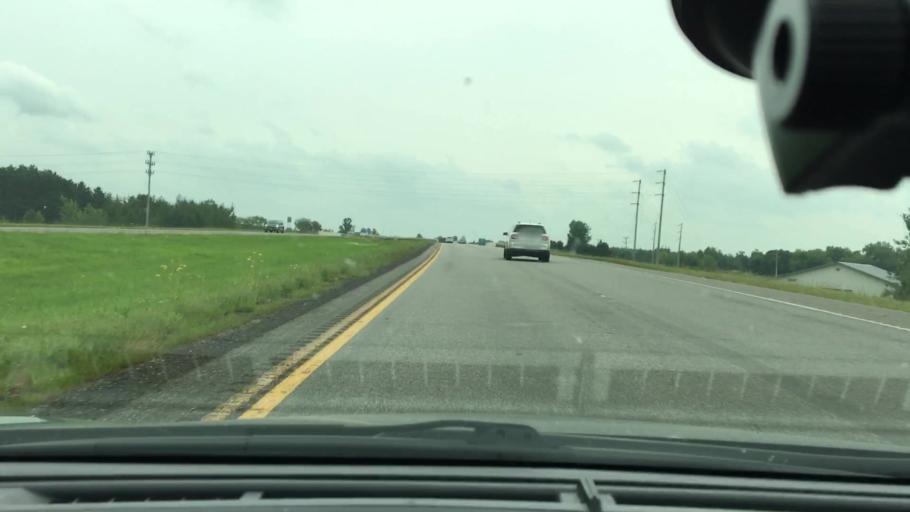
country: US
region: Minnesota
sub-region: Mille Lacs County
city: Milaca
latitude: 45.7659
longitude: -93.6427
